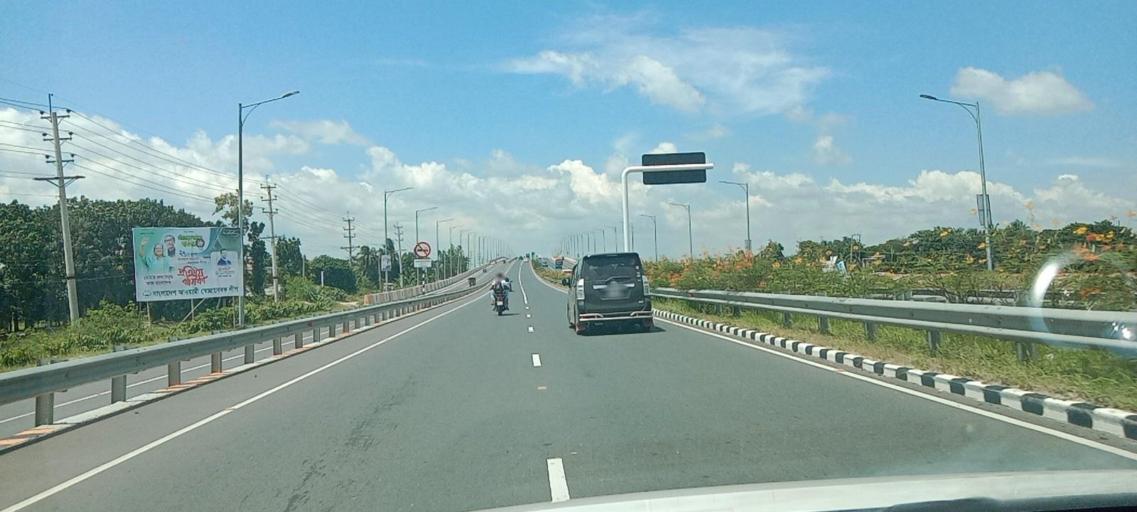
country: BD
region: Dhaka
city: Dohar
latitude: 23.5092
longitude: 90.2759
